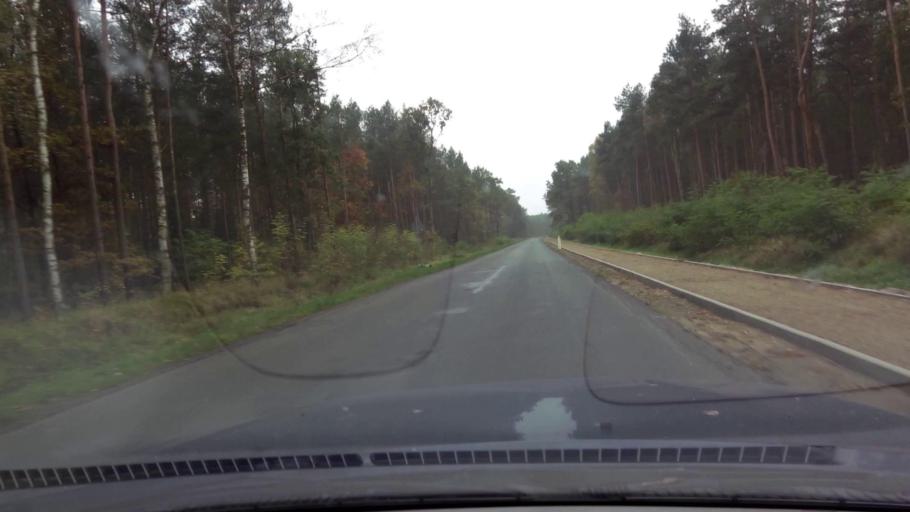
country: PL
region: West Pomeranian Voivodeship
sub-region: Powiat goleniowski
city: Goleniow
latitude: 53.5487
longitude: 14.7745
